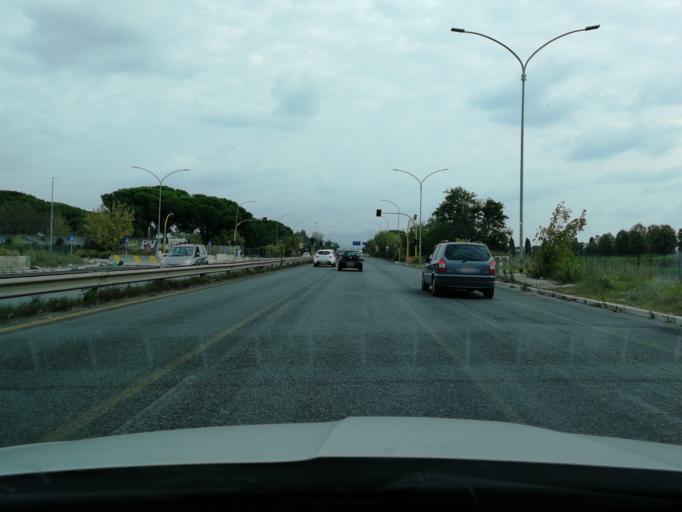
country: IT
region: Latium
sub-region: Citta metropolitana di Roma Capitale
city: Ciampino
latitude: 41.8466
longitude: 12.5784
